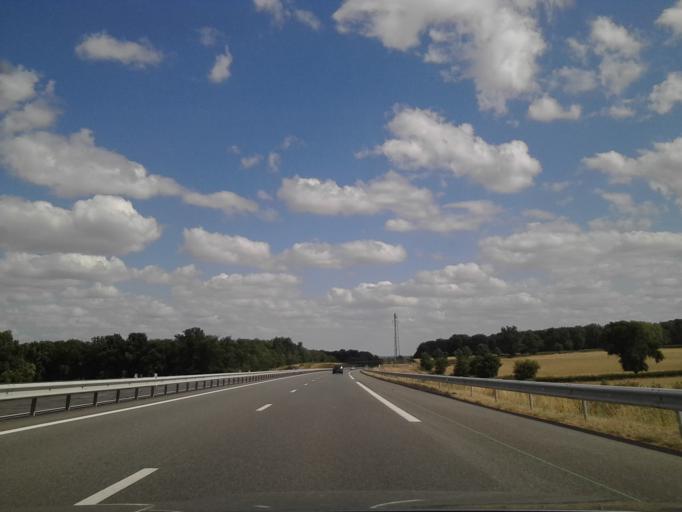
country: FR
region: Auvergne
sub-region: Departement de l'Allier
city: Vallon-en-Sully
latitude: 46.5685
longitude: 2.5381
